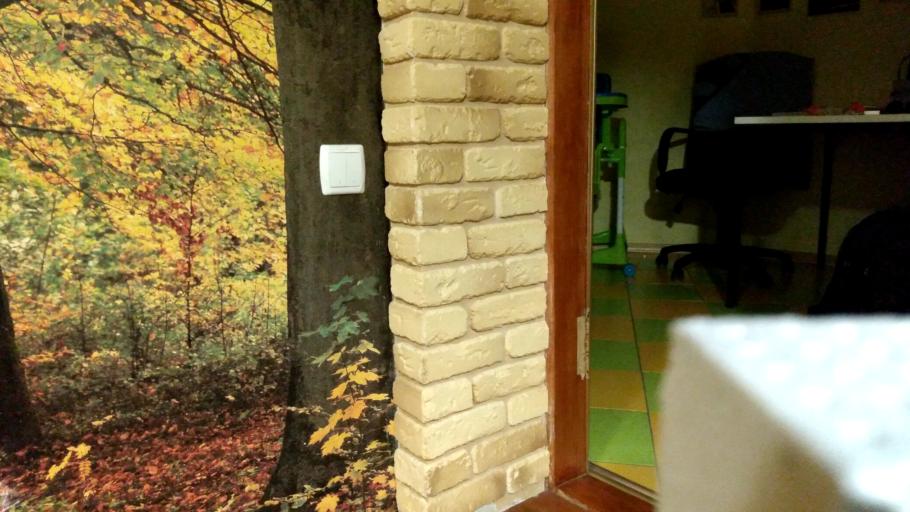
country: RU
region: Arkhangelskaya
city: Kargopol'
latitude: 61.5673
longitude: 37.7559
